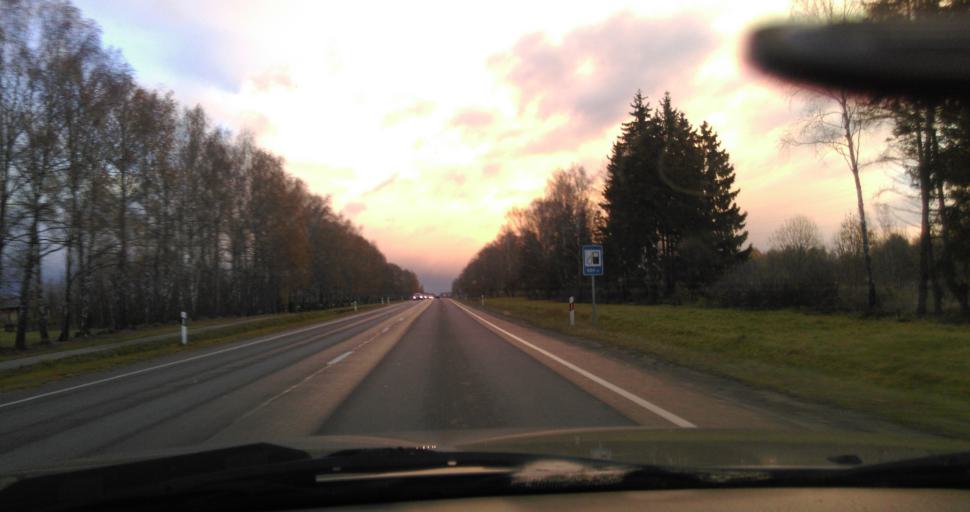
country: LT
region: Utenos apskritis
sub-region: Utena
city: Utena
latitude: 55.5093
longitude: 25.6348
